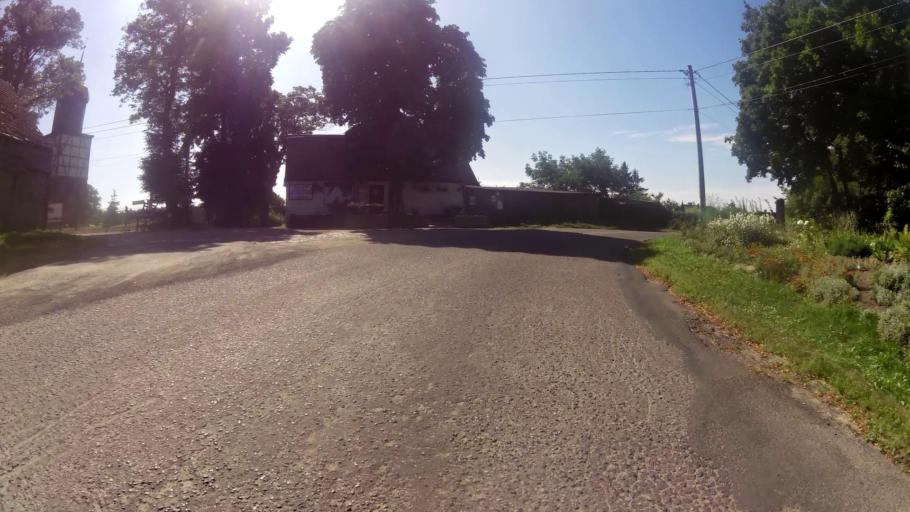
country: PL
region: West Pomeranian Voivodeship
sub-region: Powiat stargardzki
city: Insko
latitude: 53.4442
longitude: 15.6460
